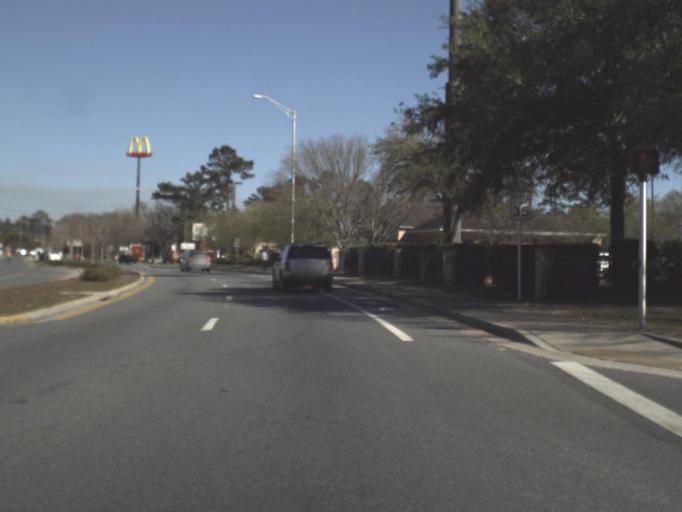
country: US
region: Florida
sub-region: Leon County
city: Tallahassee
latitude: 30.5005
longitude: -84.2504
